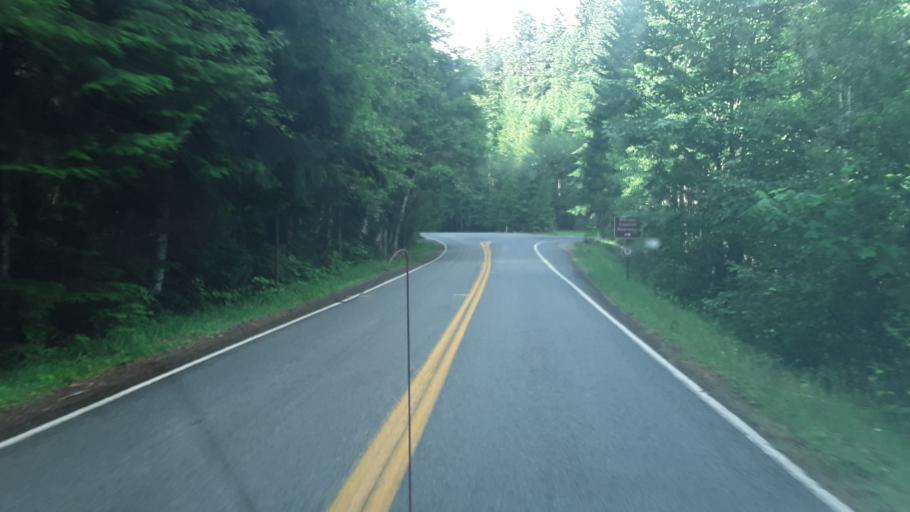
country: US
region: Washington
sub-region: Pierce County
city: Buckley
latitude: 46.7555
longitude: -121.5562
